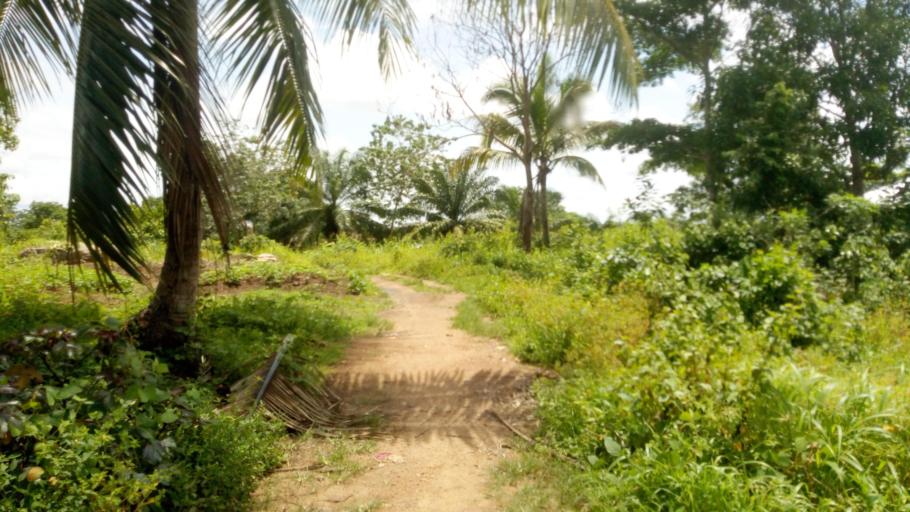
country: SL
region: Northern Province
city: Magburaka
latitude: 8.7229
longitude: -11.9565
